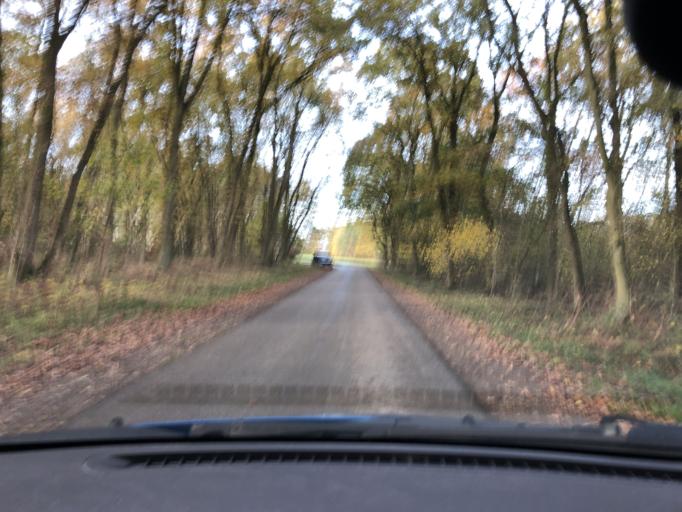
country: DE
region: Lower Saxony
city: Brietlingen
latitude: 53.3582
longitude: 10.4425
